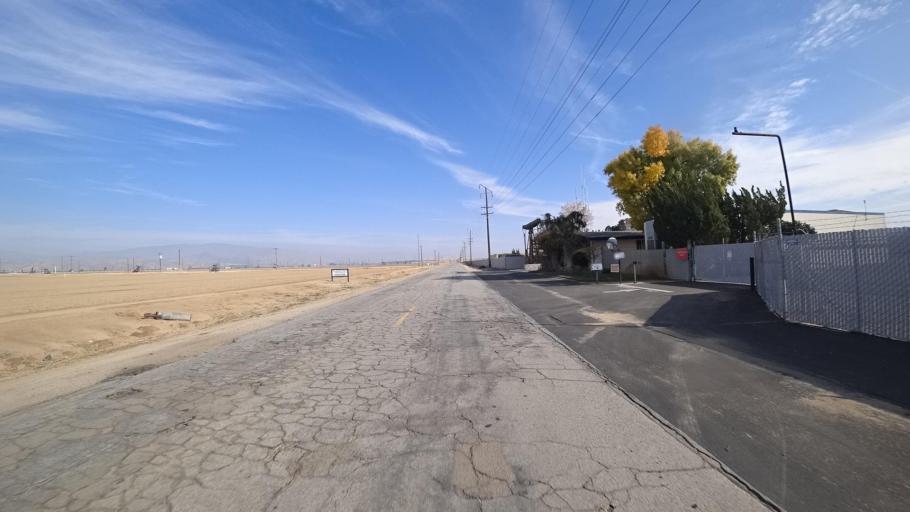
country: US
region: California
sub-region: Kern County
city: Lamont
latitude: 35.3111
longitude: -118.8319
